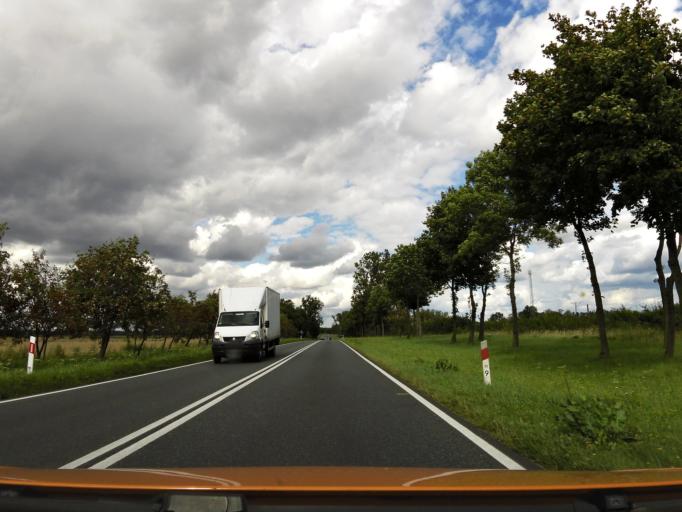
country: PL
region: West Pomeranian Voivodeship
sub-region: Powiat gryficki
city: Ploty
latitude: 53.7463
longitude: 15.2165
